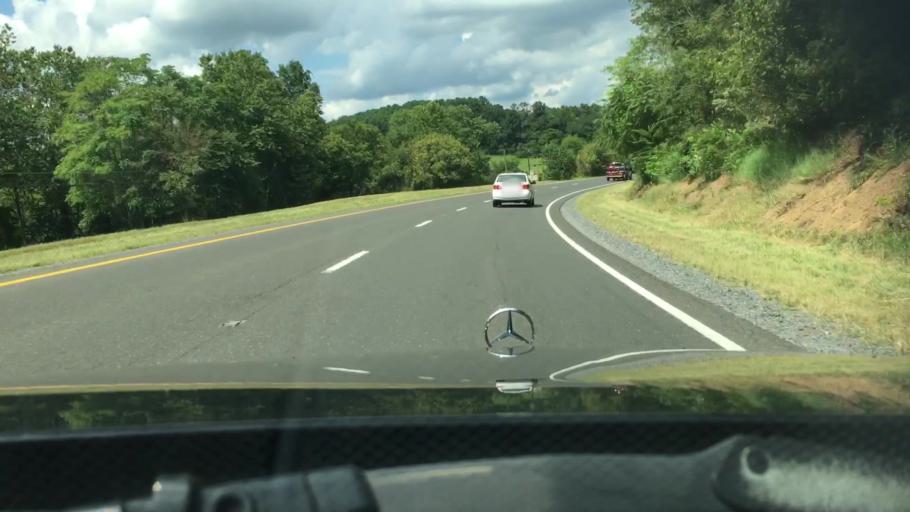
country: US
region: Virginia
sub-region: City of Winchester
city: Winchester
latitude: 39.2516
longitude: -78.2144
